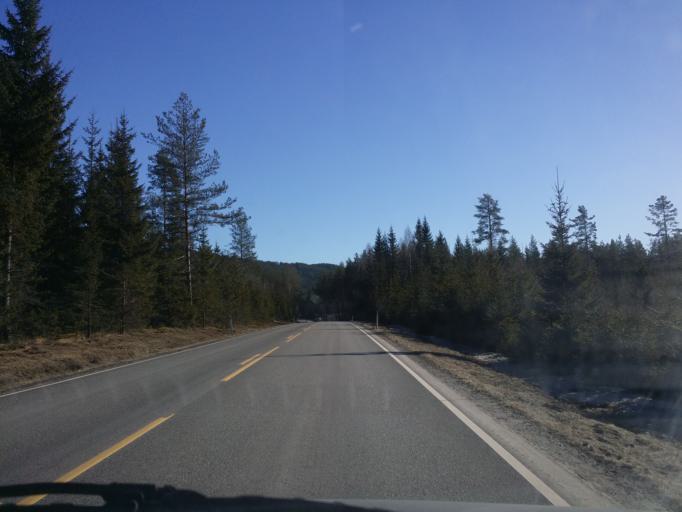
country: NO
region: Buskerud
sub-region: Ringerike
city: Honefoss
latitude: 60.2977
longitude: 10.1788
